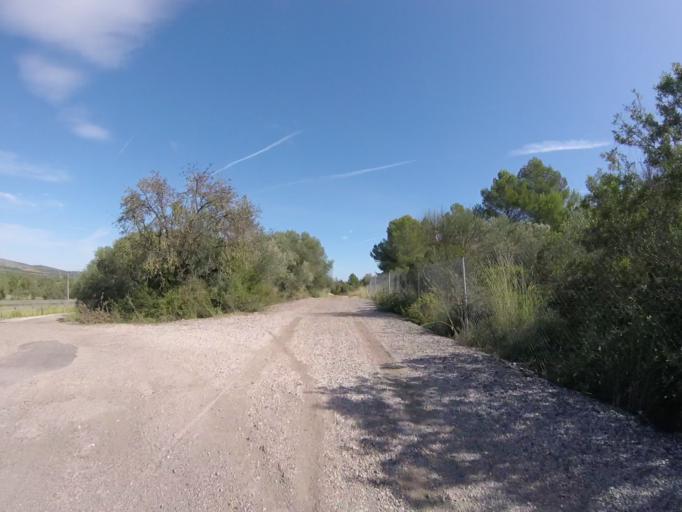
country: ES
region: Valencia
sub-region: Provincia de Castello
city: Santa Magdalena de Pulpis
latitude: 40.3910
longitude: 0.3523
